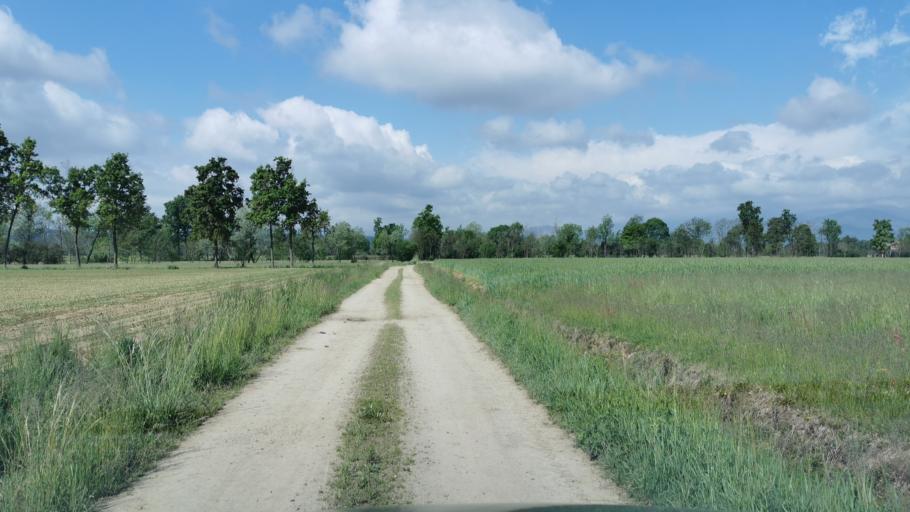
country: IT
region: Piedmont
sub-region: Provincia di Torino
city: Front
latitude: 45.2835
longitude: 7.7007
